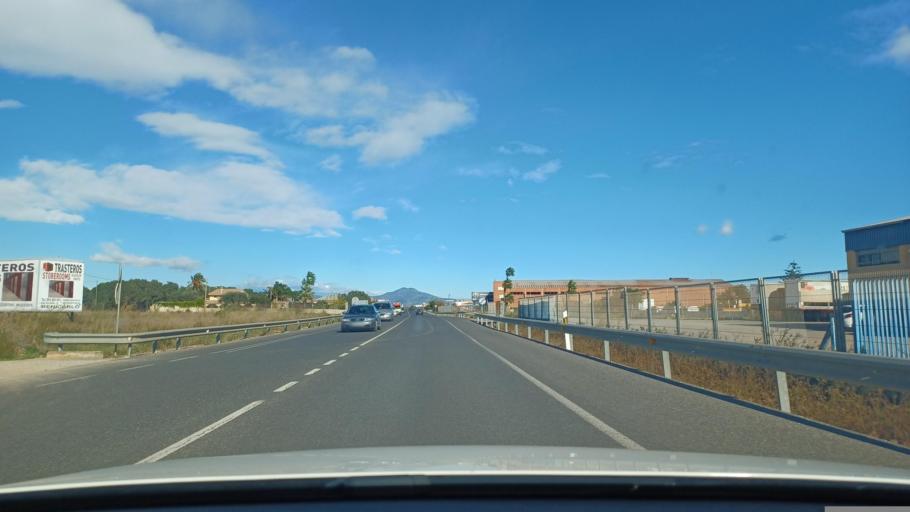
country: ES
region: Valencia
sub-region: Provincia de Castello
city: Benicarlo
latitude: 40.4337
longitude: 0.4385
